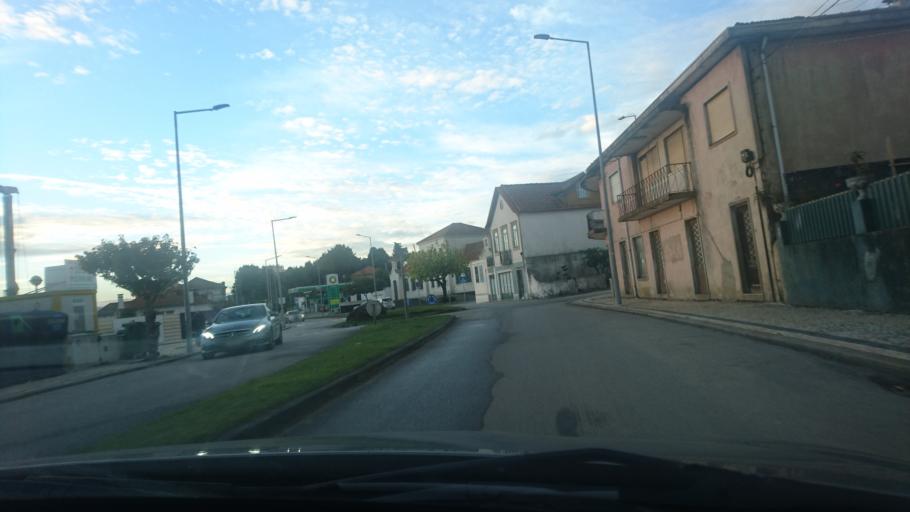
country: PT
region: Aveiro
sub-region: Sao Joao da Madeira
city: Sao Joao da Madeira
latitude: 40.8947
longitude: -8.4907
